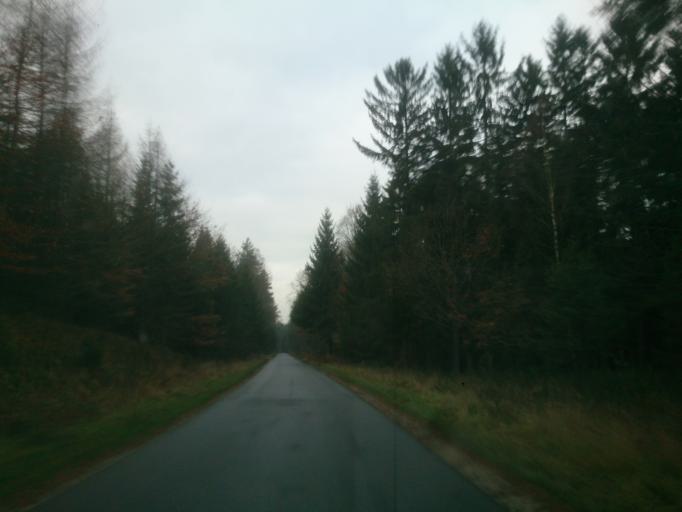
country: PL
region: Pomeranian Voivodeship
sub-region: Powiat slupski
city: Kepice
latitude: 54.2294
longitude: 16.7753
